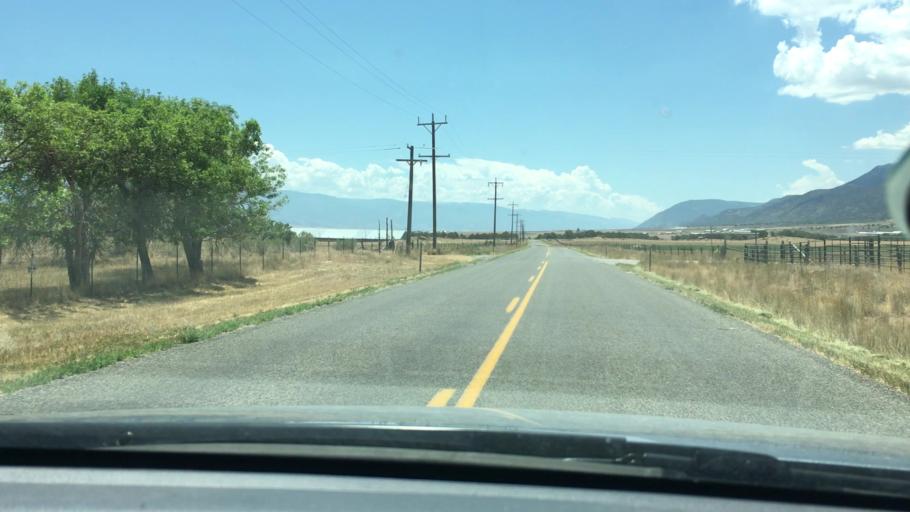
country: US
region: Utah
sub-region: Sanpete County
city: Fountain Green
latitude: 39.5993
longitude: -111.6435
